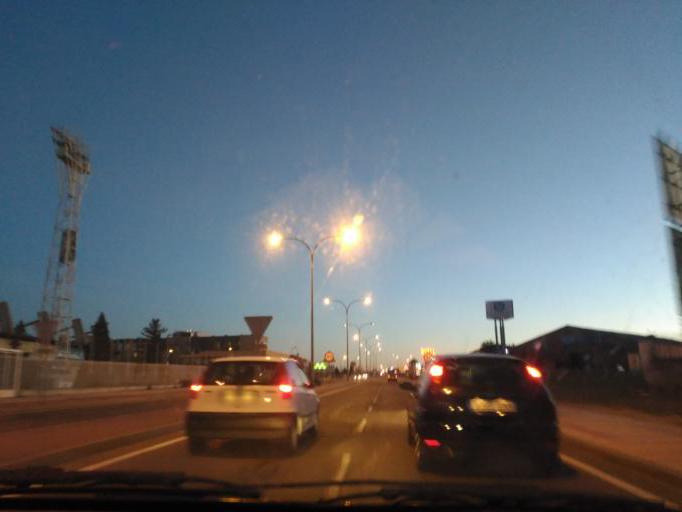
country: ES
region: Castille and Leon
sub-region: Provincia de Salamanca
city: Villares de la Reina
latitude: 40.9957
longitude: -5.6663
